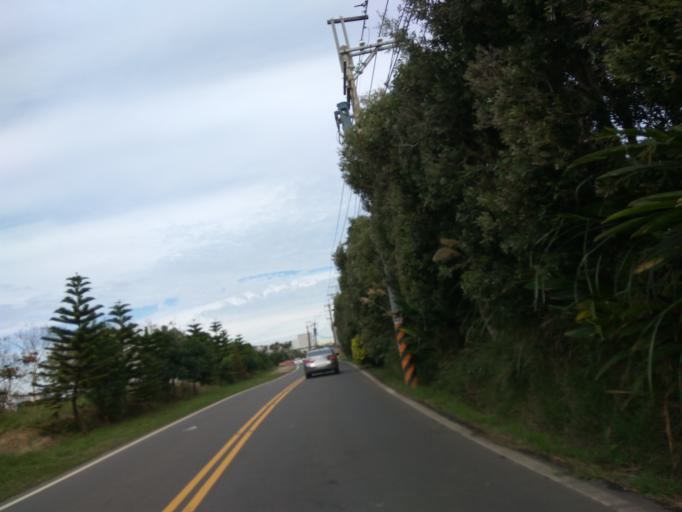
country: TW
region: Taiwan
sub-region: Hsinchu
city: Zhubei
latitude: 24.9577
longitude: 121.1197
